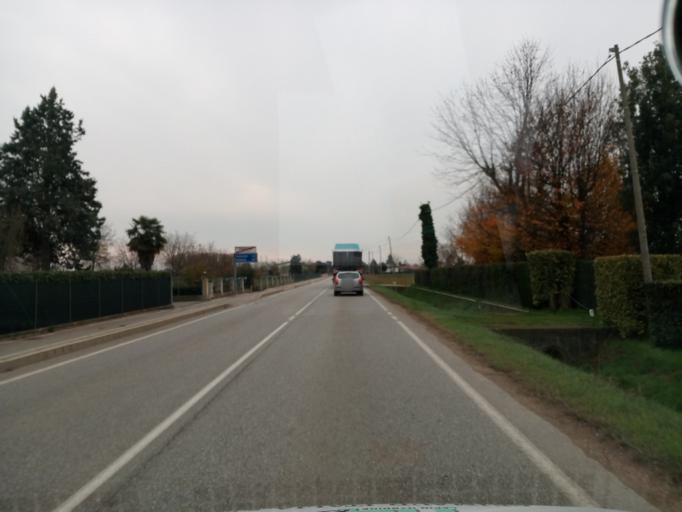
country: IT
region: Veneto
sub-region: Provincia di Treviso
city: Fanzolo
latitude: 45.7159
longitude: 12.0149
